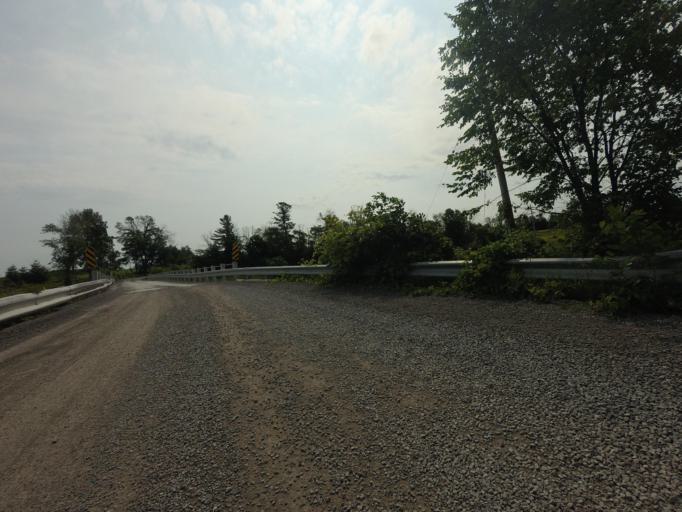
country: CA
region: Ontario
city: Arnprior
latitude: 45.4211
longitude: -76.2504
